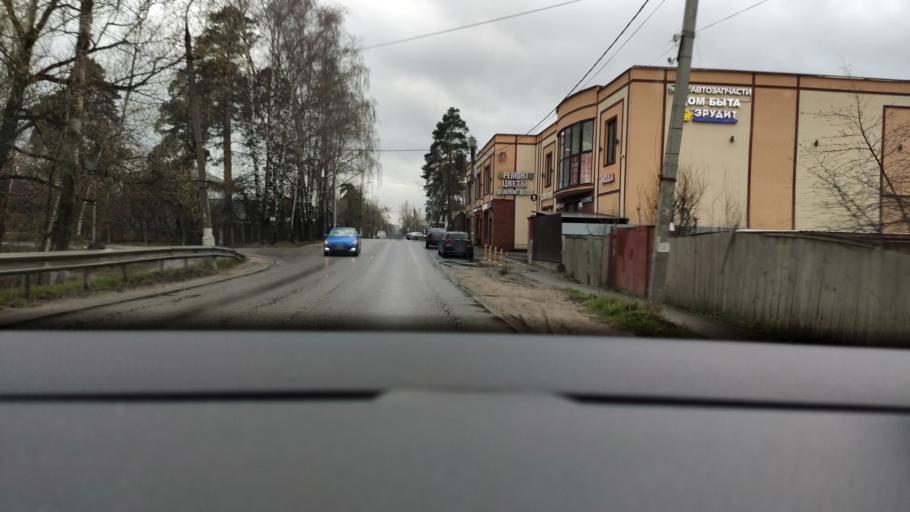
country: RU
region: Moskovskaya
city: Saltykovka
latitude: 55.7749
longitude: 37.9001
